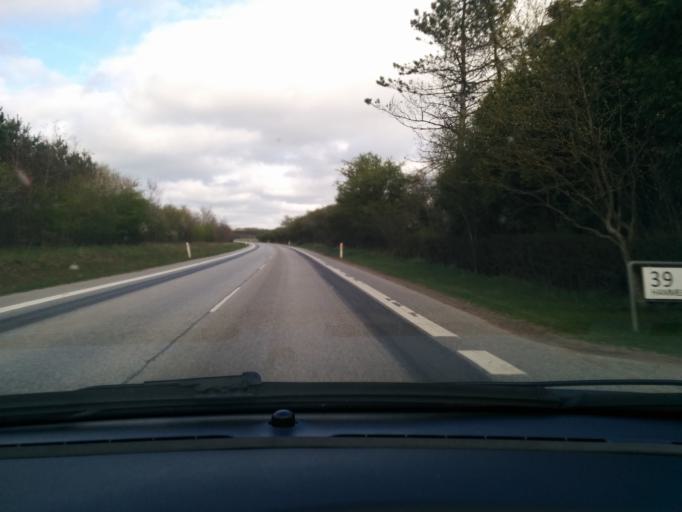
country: DK
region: Central Jutland
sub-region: Favrskov Kommune
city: Hadsten
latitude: 56.3184
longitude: 10.0023
